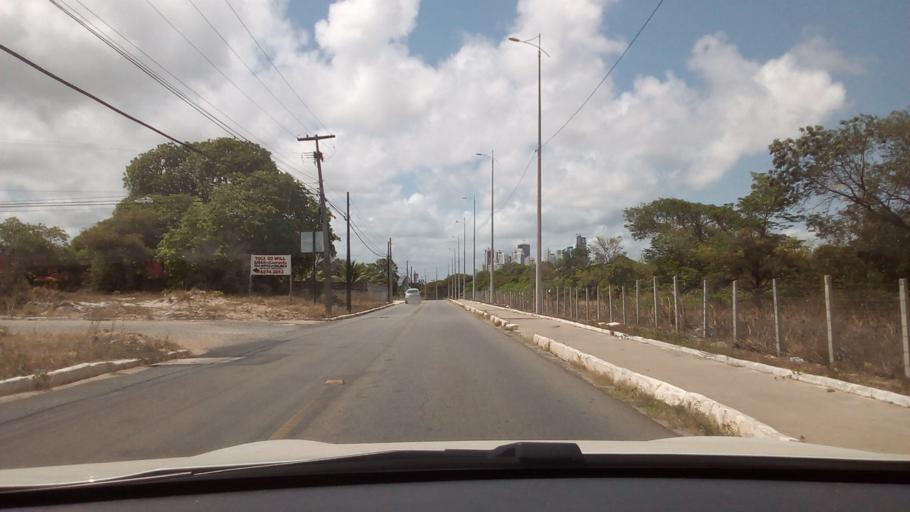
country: BR
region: Paraiba
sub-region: Joao Pessoa
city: Joao Pessoa
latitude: -7.1463
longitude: -34.8124
